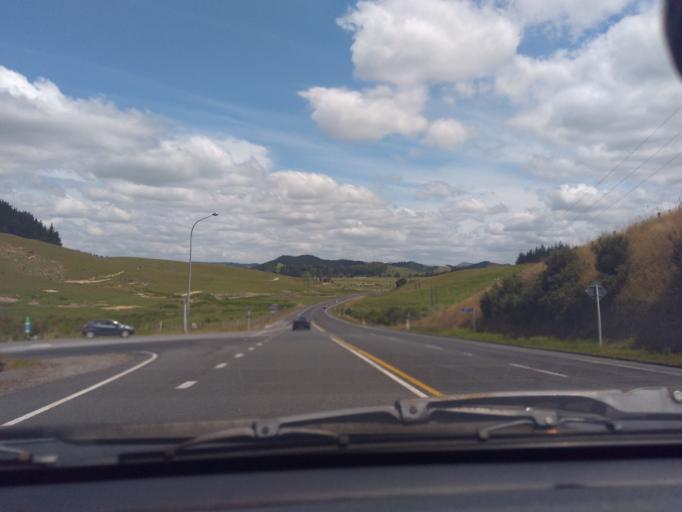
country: NZ
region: Northland
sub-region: Far North District
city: Kerikeri
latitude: -35.2834
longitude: 173.9563
